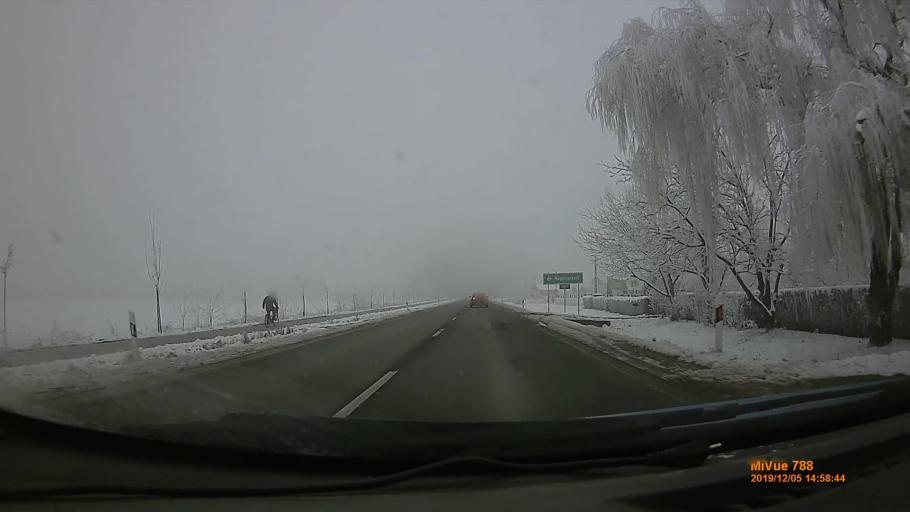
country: HU
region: Szabolcs-Szatmar-Bereg
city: Nyirtelek
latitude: 48.0512
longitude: 21.5671
